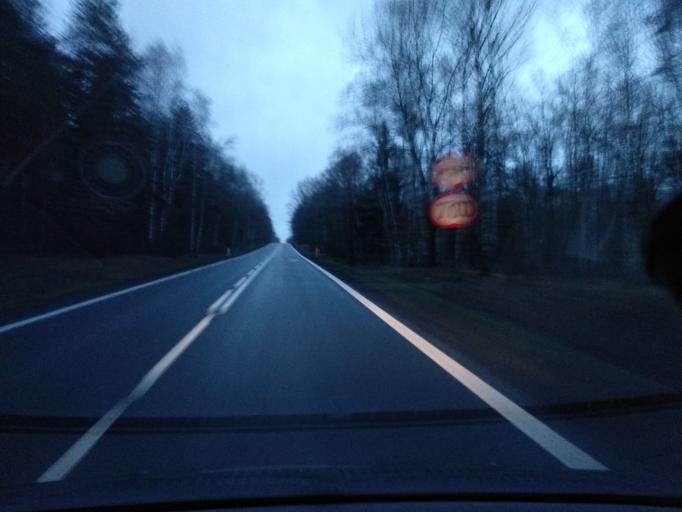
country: PL
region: Lower Silesian Voivodeship
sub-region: Powiat legnicki
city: Prochowice
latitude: 51.2472
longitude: 16.4070
